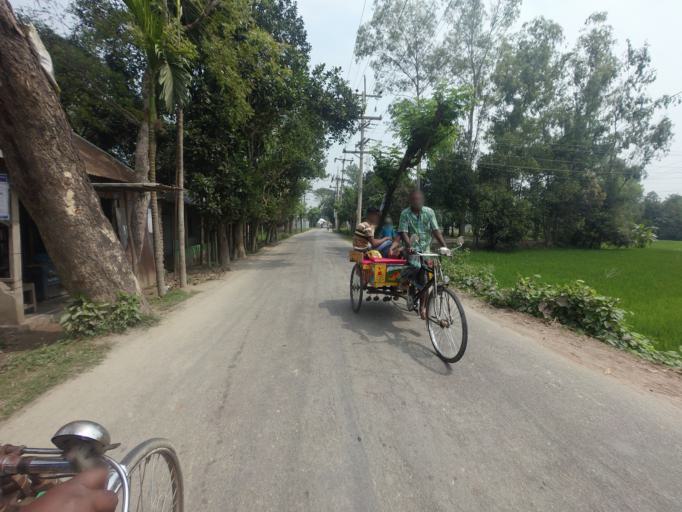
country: BD
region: Rajshahi
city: Sirajganj
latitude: 24.3902
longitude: 89.6868
